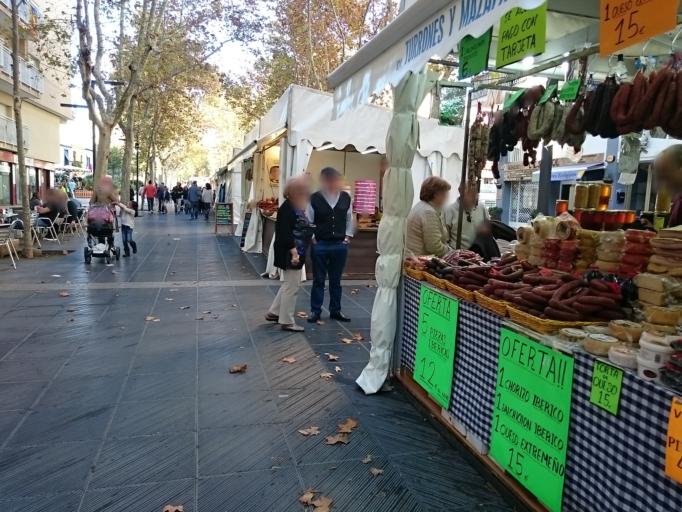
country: ES
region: Catalonia
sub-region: Provincia de Barcelona
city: Vilanova i la Geltru
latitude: 41.2163
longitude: 1.7291
